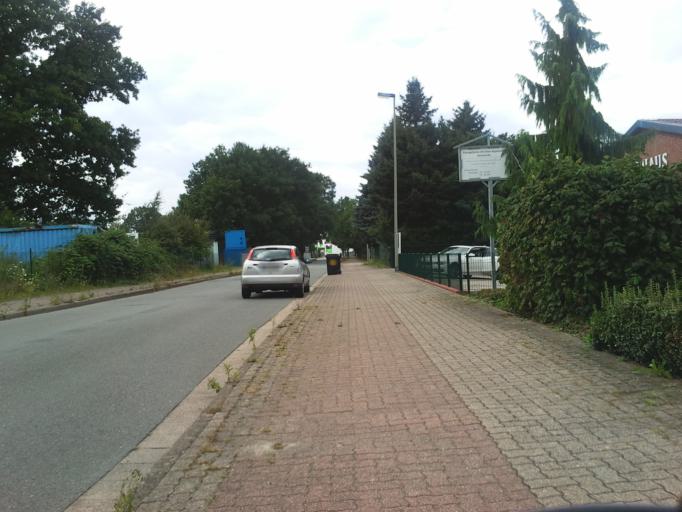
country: DE
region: Lower Saxony
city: Nienburg
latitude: 52.6391
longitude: 9.2402
